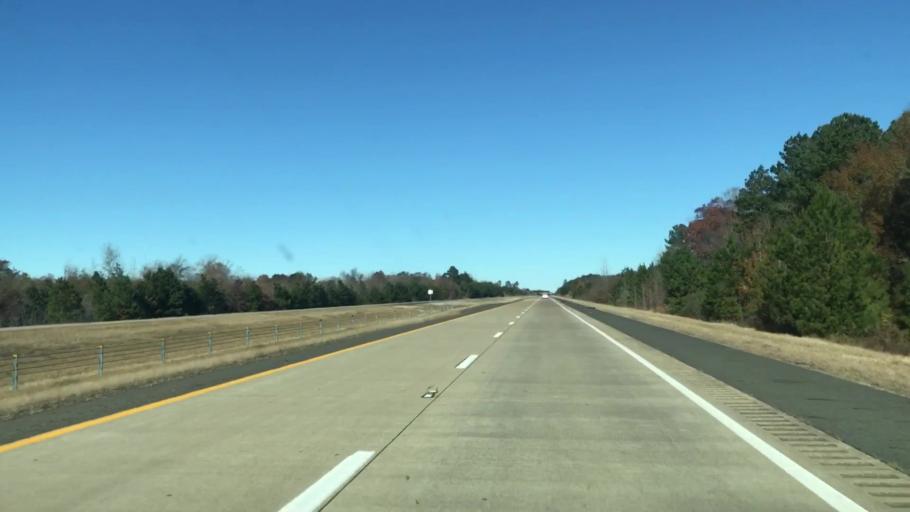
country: US
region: Texas
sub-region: Bowie County
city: Texarkana
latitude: 33.3004
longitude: -93.9292
